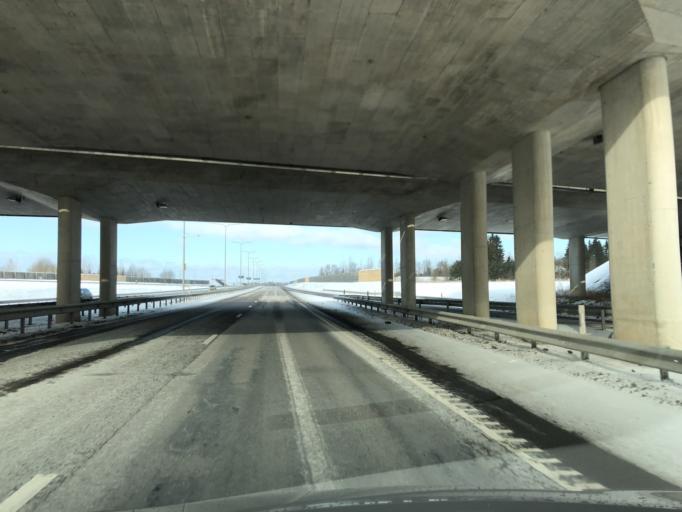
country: EE
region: Jaervamaa
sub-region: Paide linn
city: Paide
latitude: 58.9176
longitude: 25.6201
